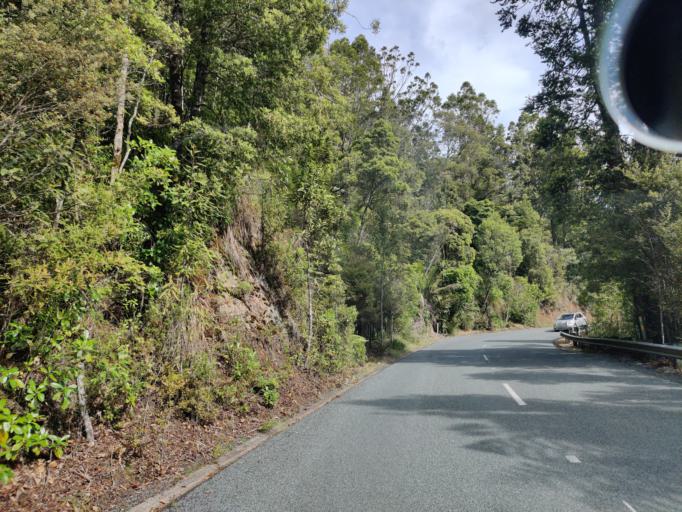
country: NZ
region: Northland
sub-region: Kaipara District
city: Dargaville
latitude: -35.6477
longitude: 173.5604
